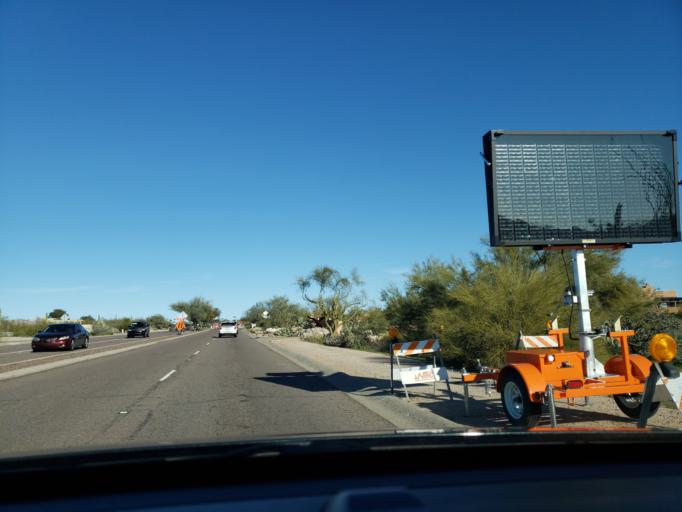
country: US
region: Arizona
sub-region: Maricopa County
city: Carefree
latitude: 33.8184
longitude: -111.8904
